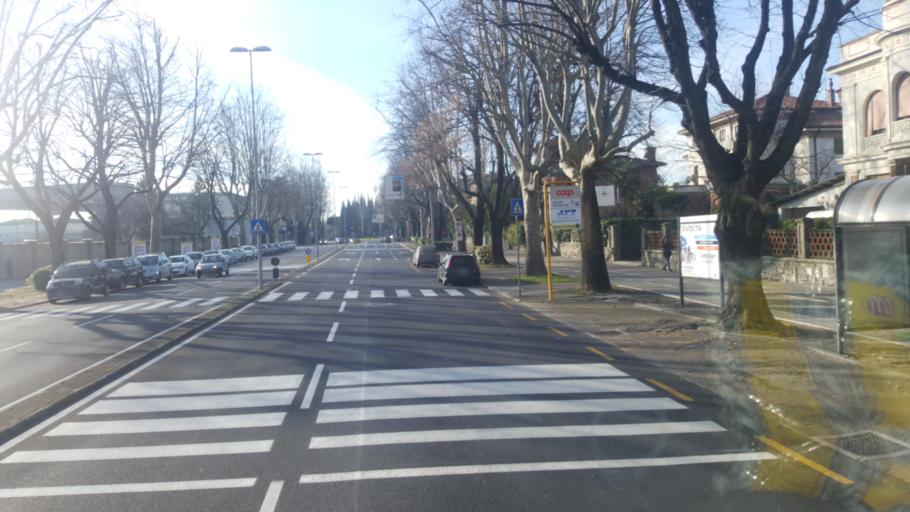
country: IT
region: Friuli Venezia Giulia
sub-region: Provincia di Gorizia
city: Monfalcone
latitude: 45.8036
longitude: 13.5321
